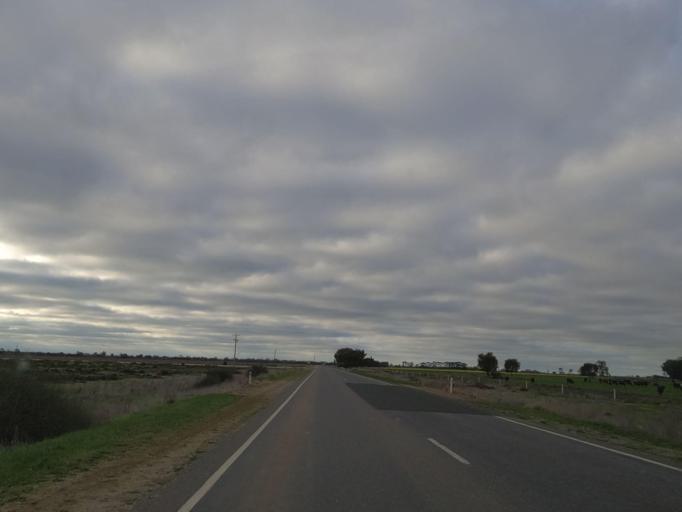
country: AU
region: Victoria
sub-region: Swan Hill
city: Swan Hill
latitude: -35.8333
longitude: 143.9431
